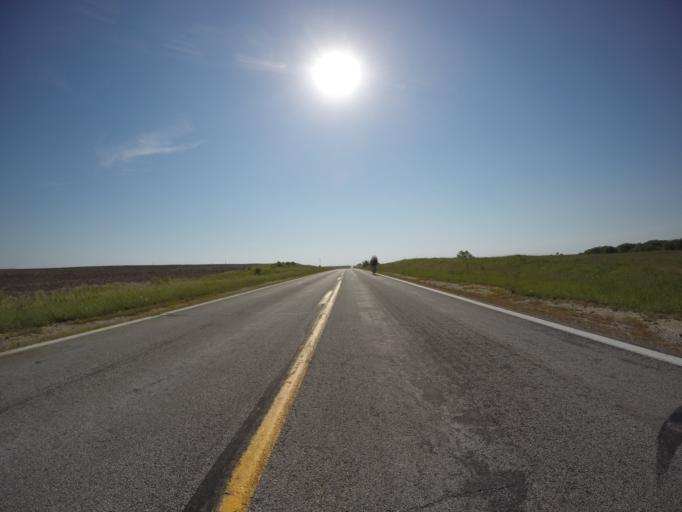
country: US
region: Nebraska
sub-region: Pawnee County
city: Pawnee City
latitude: 40.0447
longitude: -96.3726
